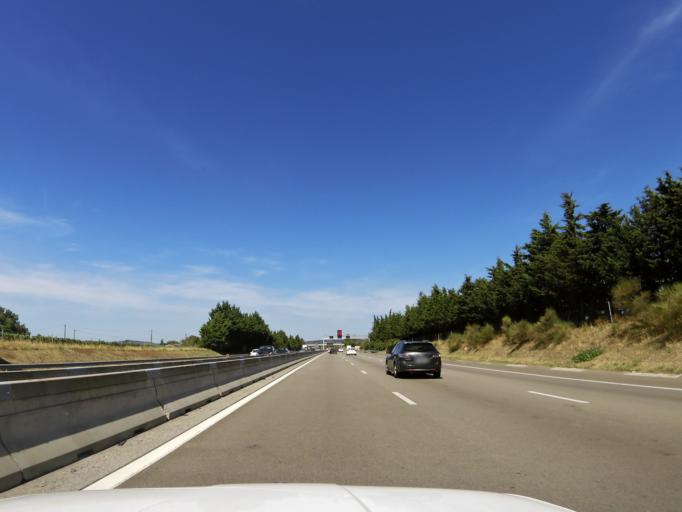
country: FR
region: Rhone-Alpes
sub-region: Departement de la Drome
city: La Roche-de-Glun
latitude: 45.0351
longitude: 4.8764
